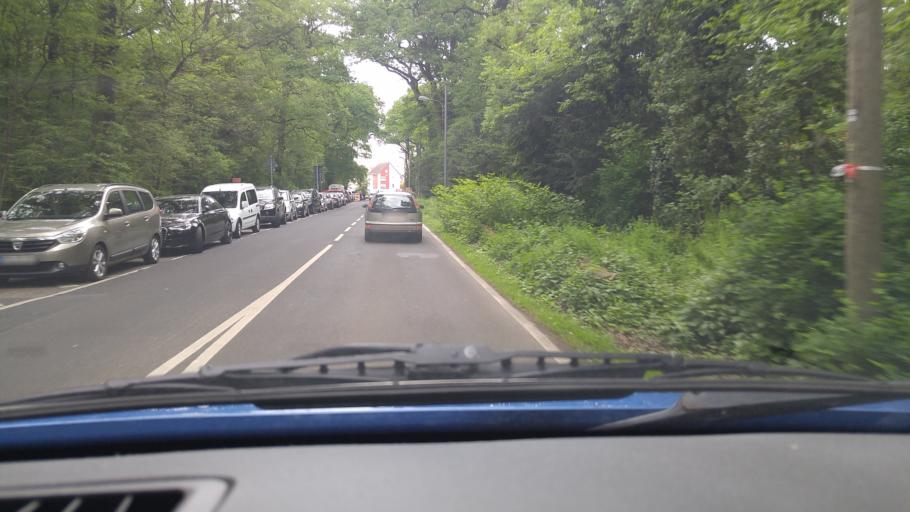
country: DE
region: Hesse
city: Niederrad
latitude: 50.0805
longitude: 8.5795
